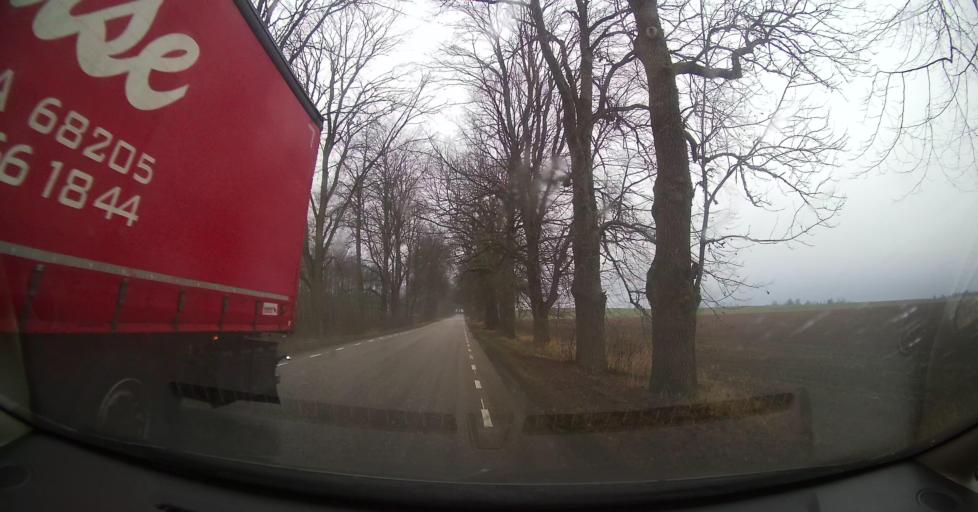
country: EE
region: Tartu
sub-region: Alatskivi vald
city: Kallaste
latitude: 58.3839
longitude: 27.0328
